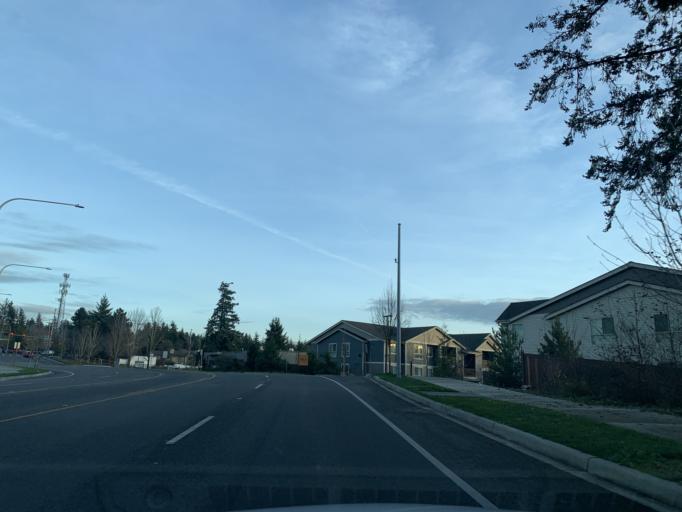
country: US
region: Washington
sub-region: King County
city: Lakeland South
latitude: 47.2828
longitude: -122.3162
